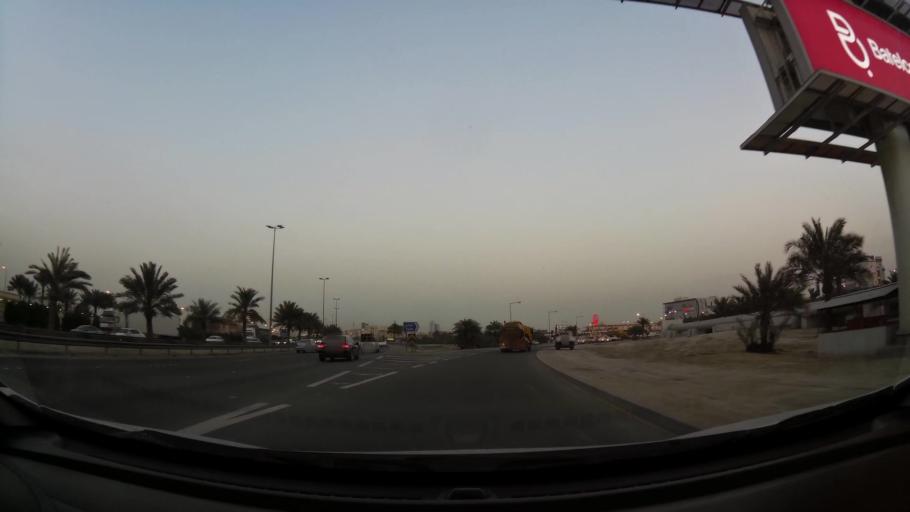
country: BH
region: Manama
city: Jidd Hafs
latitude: 26.1982
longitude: 50.5549
